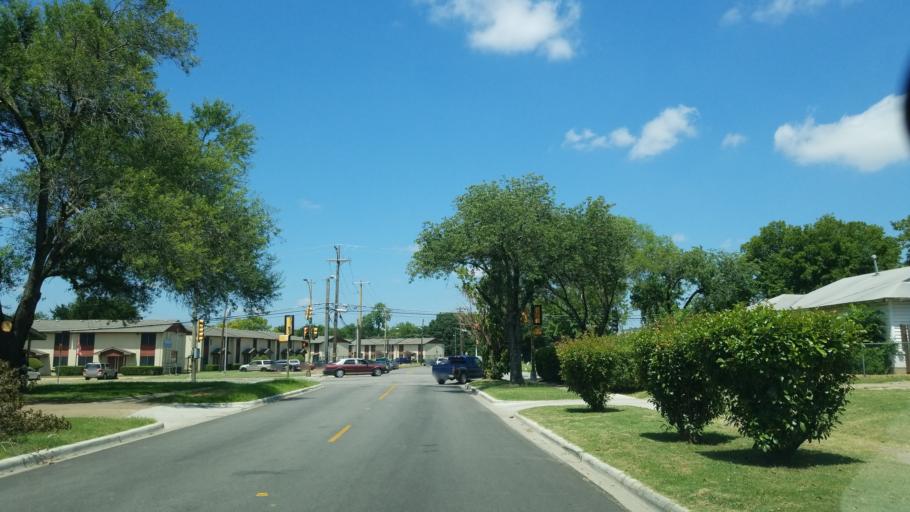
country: US
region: Texas
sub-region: Dallas County
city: Balch Springs
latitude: 32.7383
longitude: -96.6995
